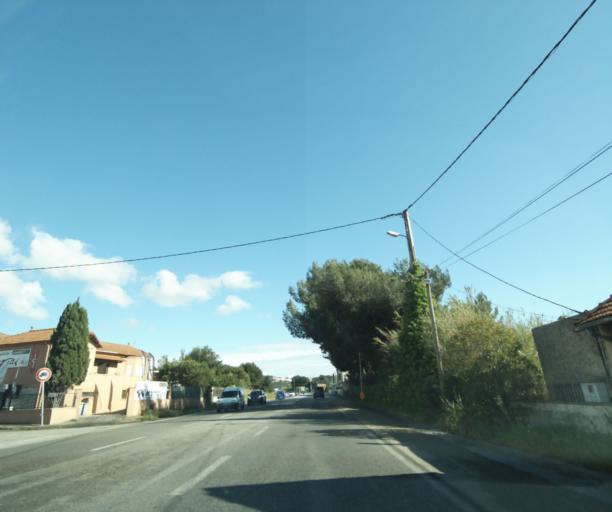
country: FR
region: Provence-Alpes-Cote d'Azur
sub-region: Departement des Bouches-du-Rhone
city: Rognac
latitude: 43.4835
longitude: 5.2241
